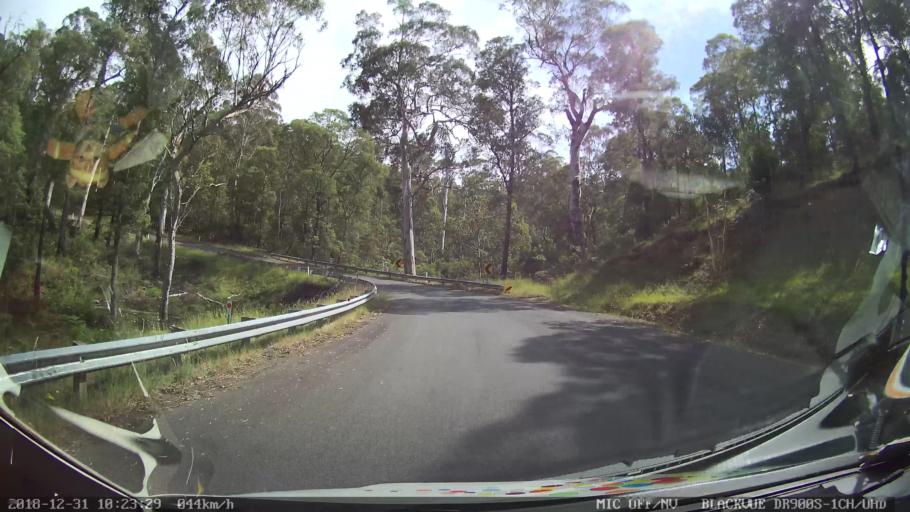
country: AU
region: New South Wales
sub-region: Snowy River
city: Jindabyne
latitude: -36.5169
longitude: 148.1446
